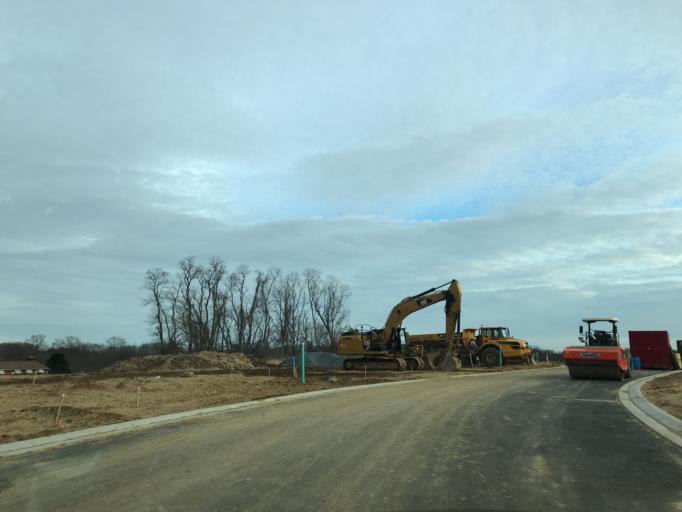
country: US
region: Maryland
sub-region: Harford County
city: Bel Air South
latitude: 39.5038
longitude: -76.3472
